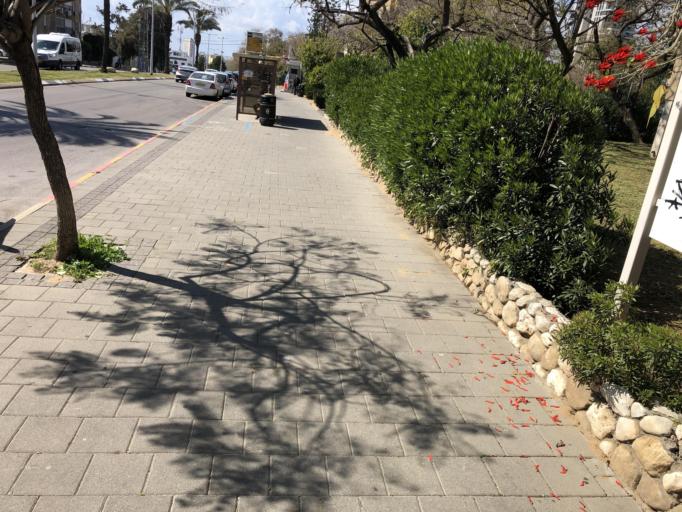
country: IL
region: Tel Aviv
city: Bat Yam
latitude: 32.0103
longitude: 34.7541
